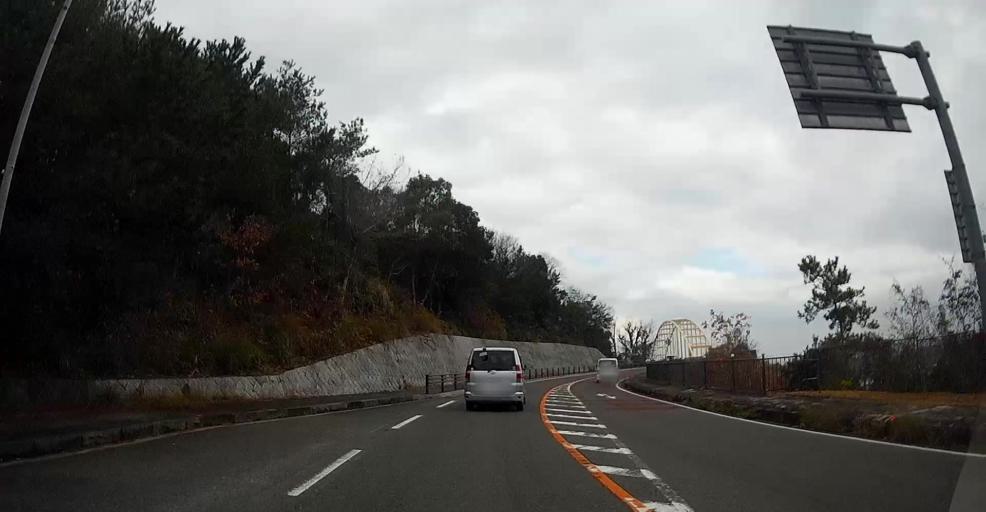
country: JP
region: Kumamoto
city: Yatsushiro
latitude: 32.5423
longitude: 130.4223
